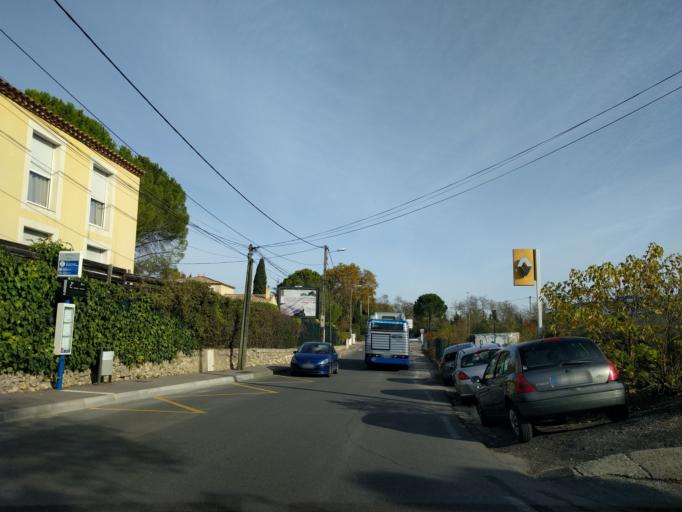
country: FR
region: Languedoc-Roussillon
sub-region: Departement de l'Herault
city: Montferrier-sur-Lez
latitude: 43.6426
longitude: 3.8595
